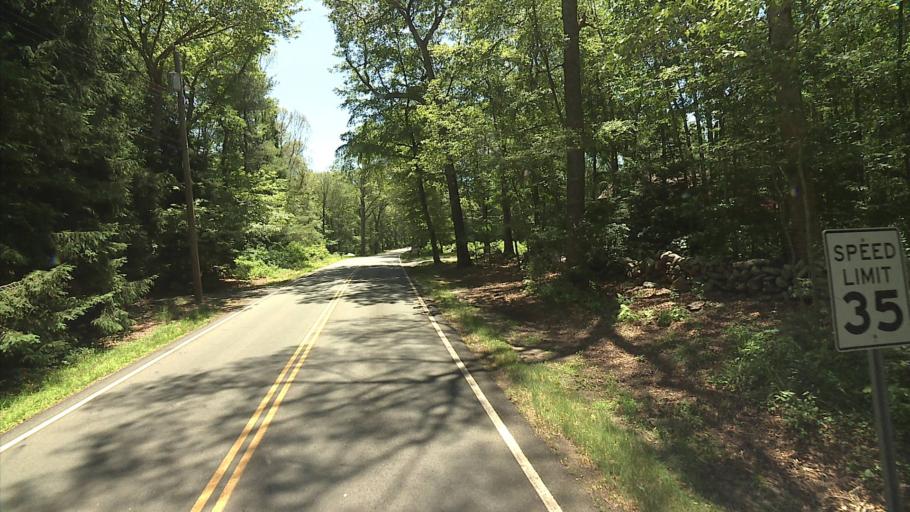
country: US
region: Connecticut
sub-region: New London County
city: Old Mystic
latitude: 41.3796
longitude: -71.9236
